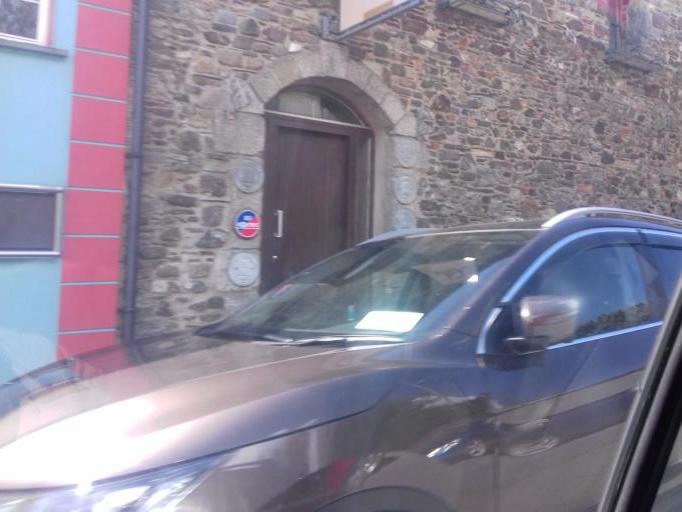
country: IE
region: Munster
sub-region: Waterford
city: Dunmore East
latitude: 52.2215
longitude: -6.9337
